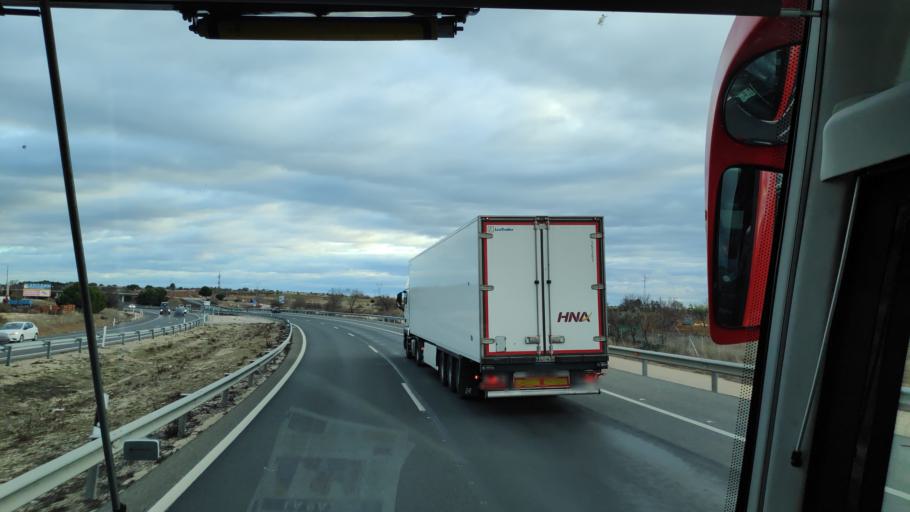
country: ES
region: Madrid
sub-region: Provincia de Madrid
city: Villarejo de Salvanes
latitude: 40.1752
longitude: -3.2955
